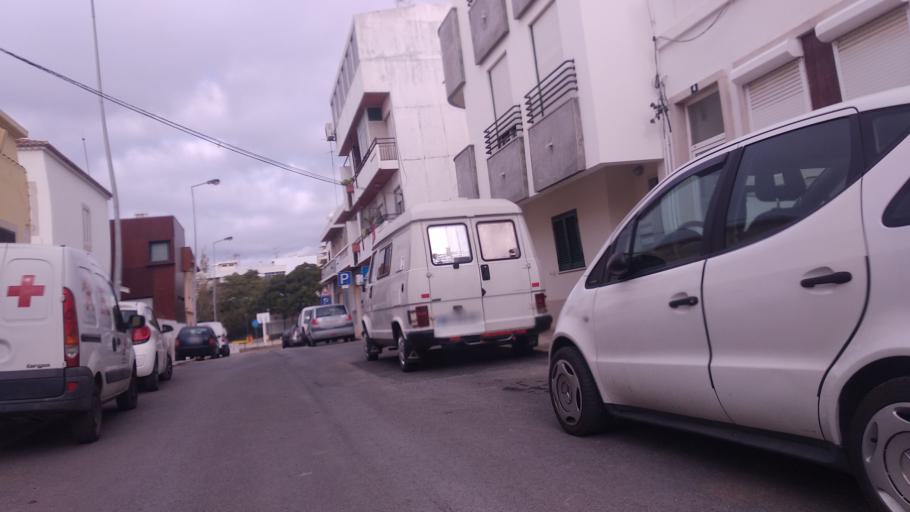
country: PT
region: Faro
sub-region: Faro
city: Faro
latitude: 37.0220
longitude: -7.9357
